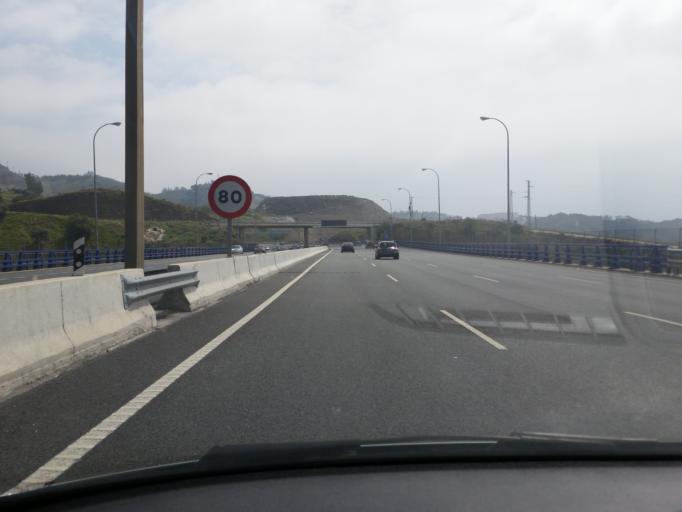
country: ES
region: Andalusia
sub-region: Provincia de Malaga
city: Malaga
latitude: 36.7415
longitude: -4.4027
